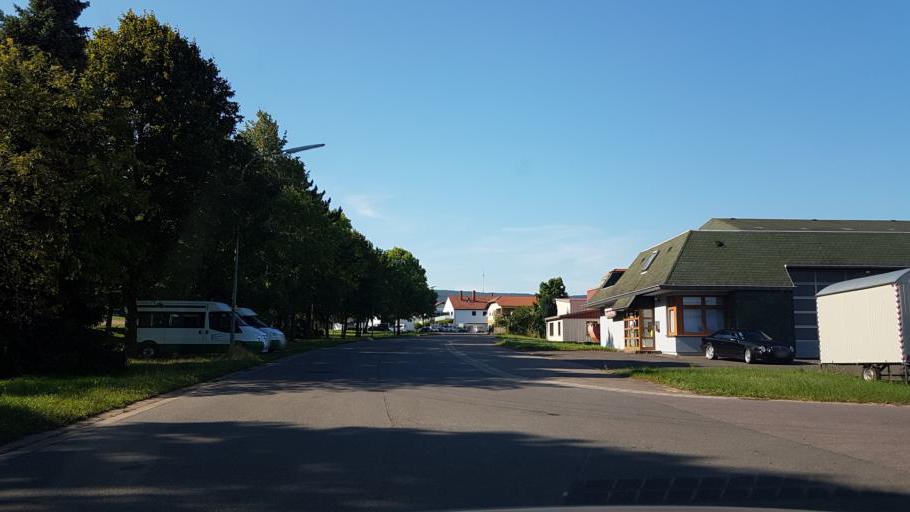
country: DE
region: Saarland
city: Weiskirchen
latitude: 49.5469
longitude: 6.8310
